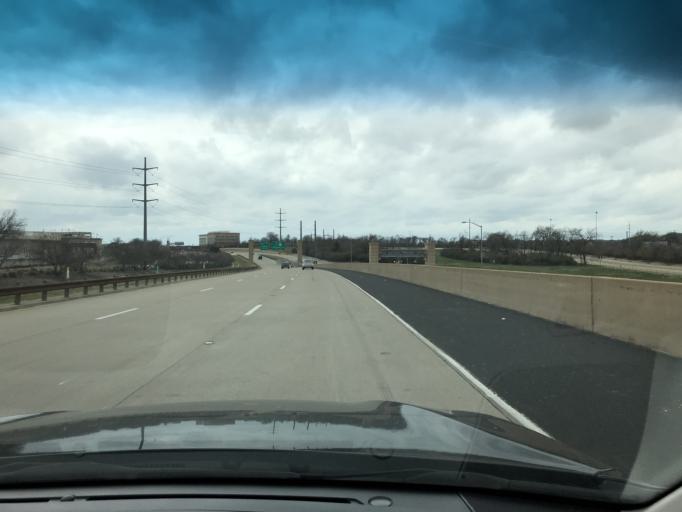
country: US
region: Texas
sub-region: Tarrant County
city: Westworth
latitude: 32.7127
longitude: -97.3990
